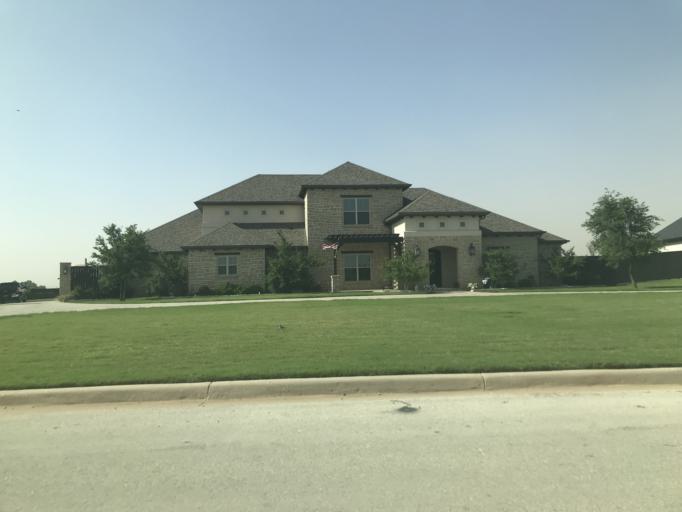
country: US
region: Texas
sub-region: Taylor County
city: Potosi
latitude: 32.3500
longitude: -99.7129
